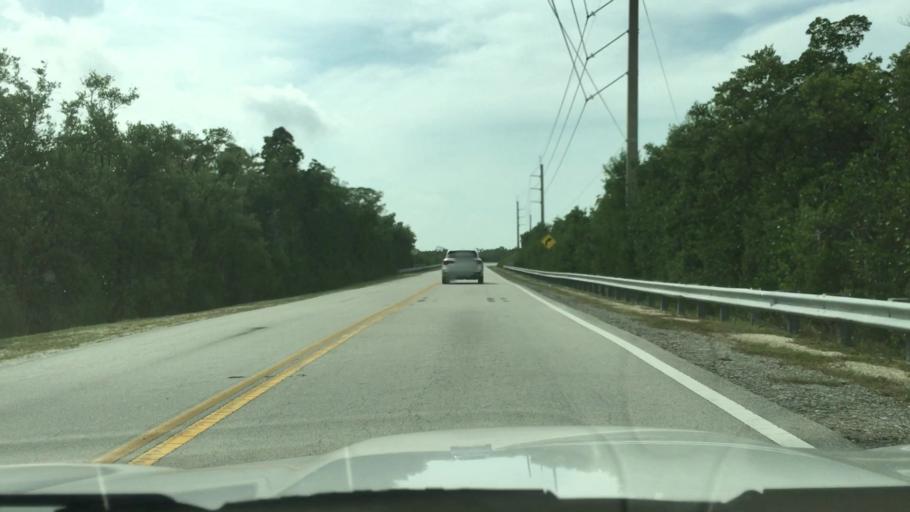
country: US
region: Florida
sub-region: Monroe County
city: North Key Largo
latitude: 25.2821
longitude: -80.3368
